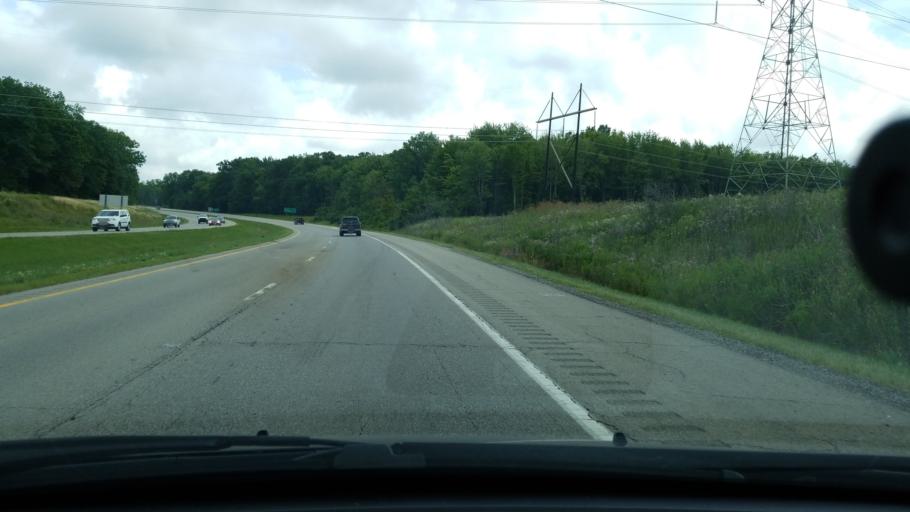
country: US
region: Ohio
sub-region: Lorain County
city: Amherst
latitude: 41.4023
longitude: -82.2682
